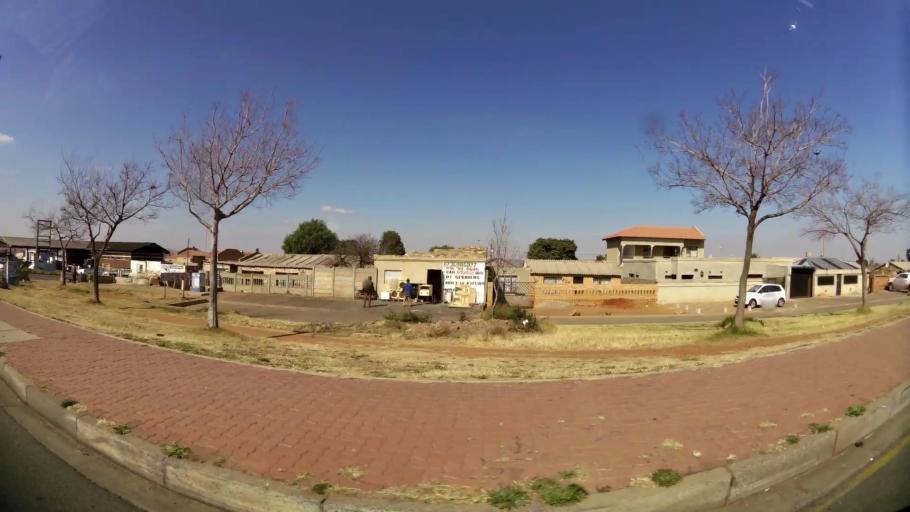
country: ZA
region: Gauteng
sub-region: City of Johannesburg Metropolitan Municipality
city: Soweto
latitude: -26.2751
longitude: 27.8699
